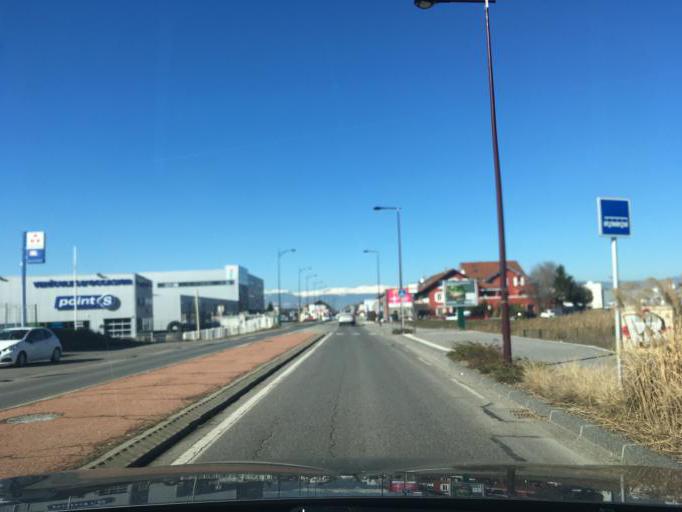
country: FR
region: Rhone-Alpes
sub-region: Departement de la Haute-Savoie
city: Cranves-Sales
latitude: 46.1839
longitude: 6.2800
